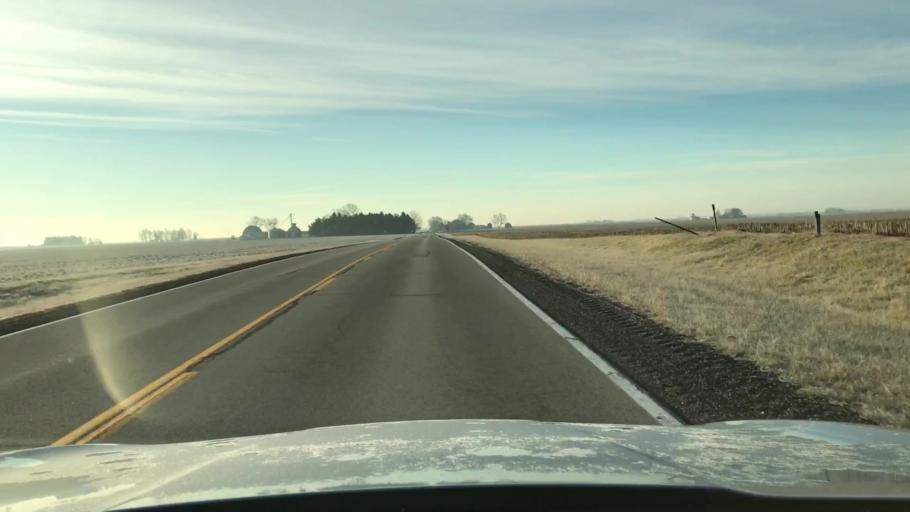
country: US
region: Illinois
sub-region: McLean County
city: Hudson
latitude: 40.6197
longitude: -88.9455
